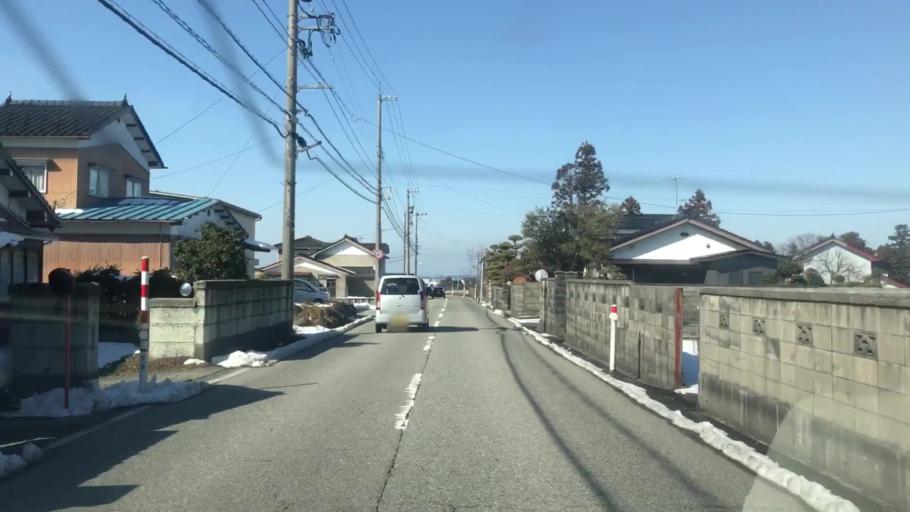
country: JP
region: Toyama
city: Toyama-shi
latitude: 36.6437
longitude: 137.2544
